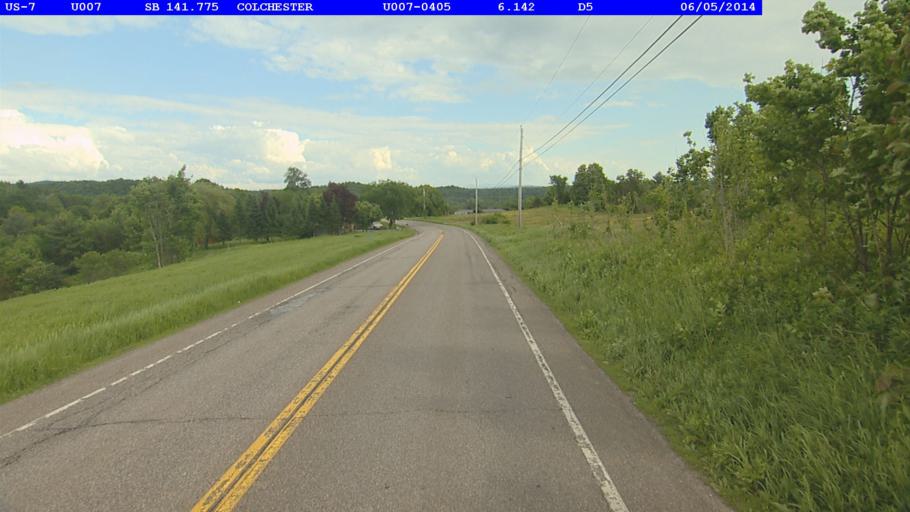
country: US
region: Vermont
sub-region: Chittenden County
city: Colchester
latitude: 44.5843
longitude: -73.1652
